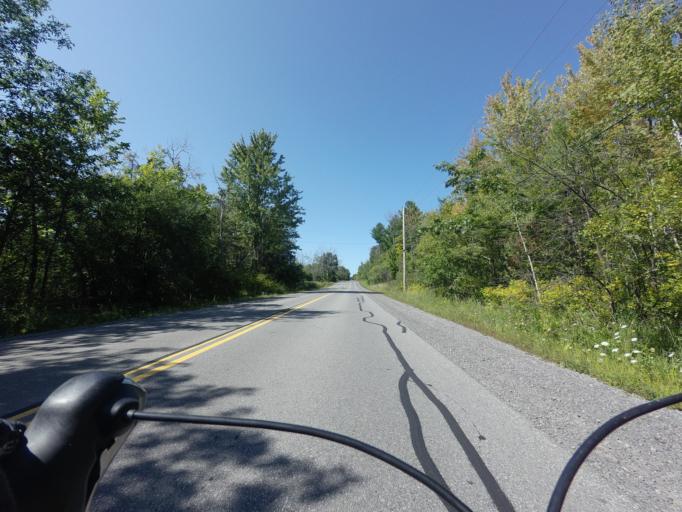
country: CA
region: Ontario
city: Bells Corners
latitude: 45.4041
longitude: -75.9253
